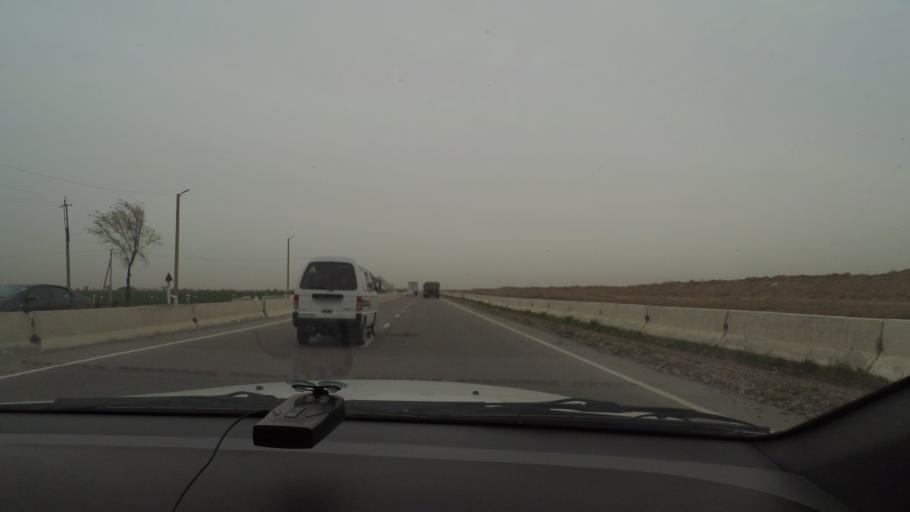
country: UZ
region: Jizzax
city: Gagarin
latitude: 40.4514
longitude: 68.2502
